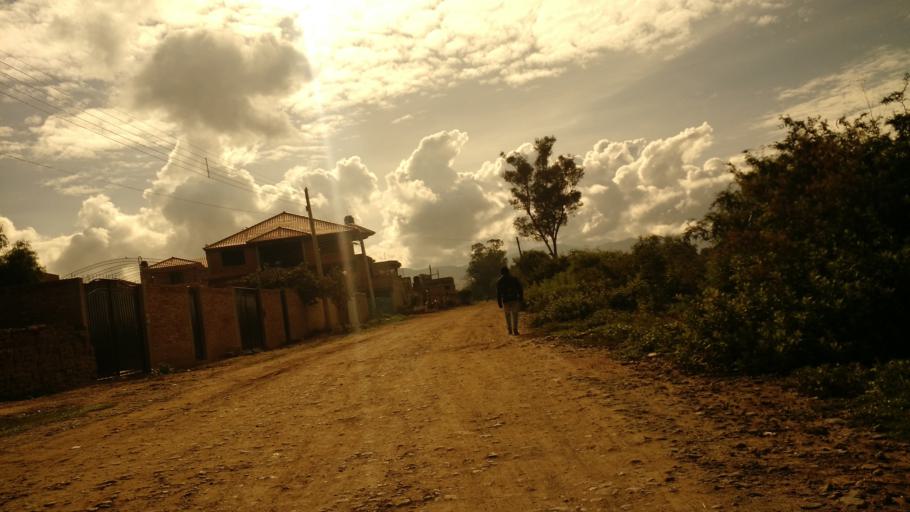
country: BO
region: Cochabamba
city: Cochabamba
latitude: -17.4537
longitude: -66.1538
